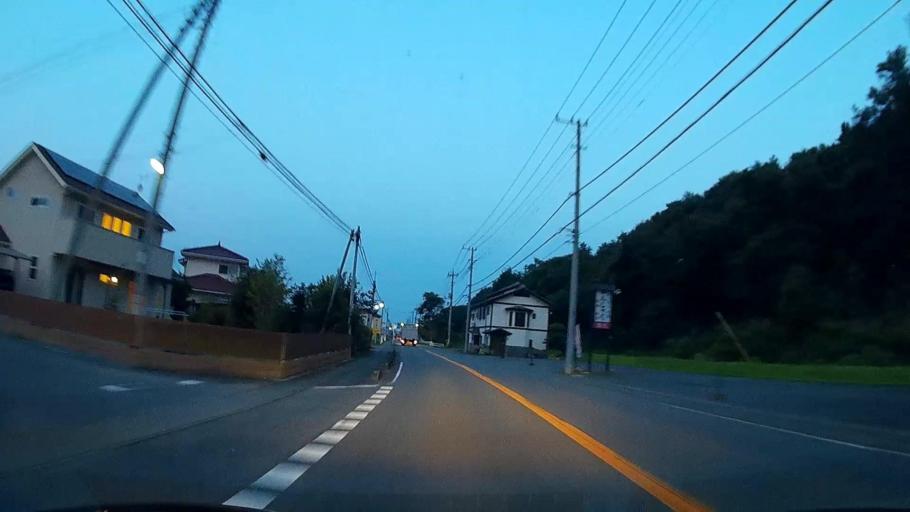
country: JP
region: Gunma
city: Annaka
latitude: 36.3513
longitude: 138.9388
